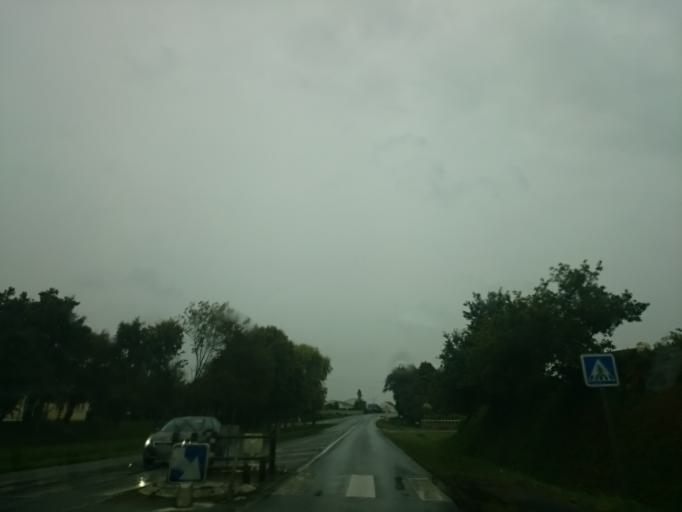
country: FR
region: Brittany
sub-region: Departement du Finistere
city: Plabennec
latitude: 48.5102
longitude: -4.4154
